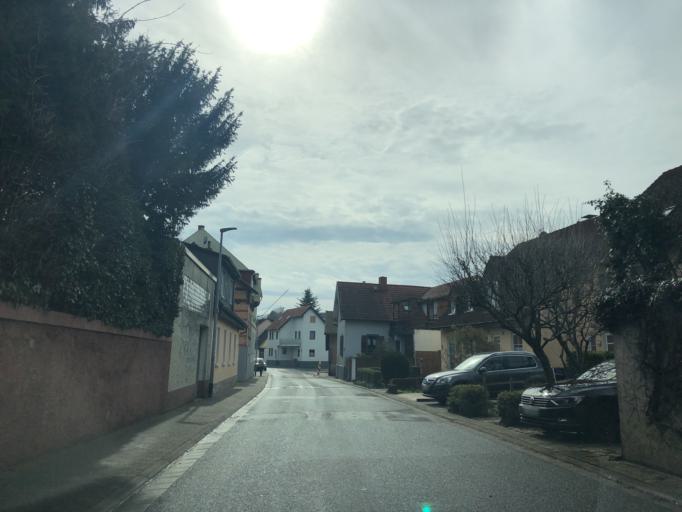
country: DE
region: Rheinland-Pfalz
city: Nierstein
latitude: 49.8725
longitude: 8.3350
